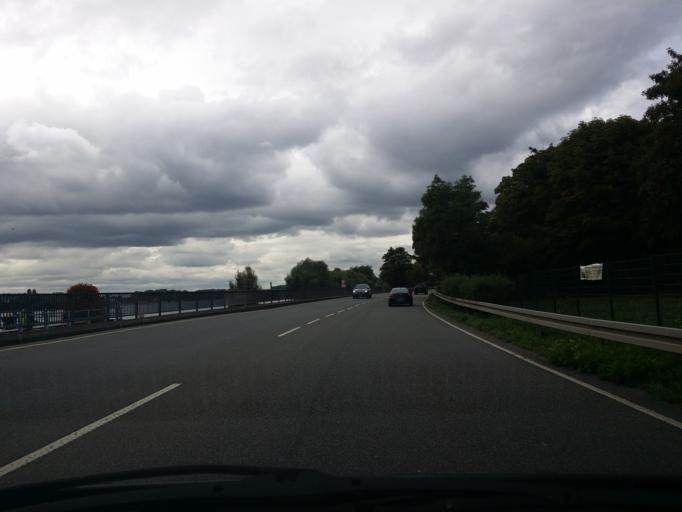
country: DE
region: Rheinland-Pfalz
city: Oestrich-Winkel
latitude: 50.0032
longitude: 8.0301
